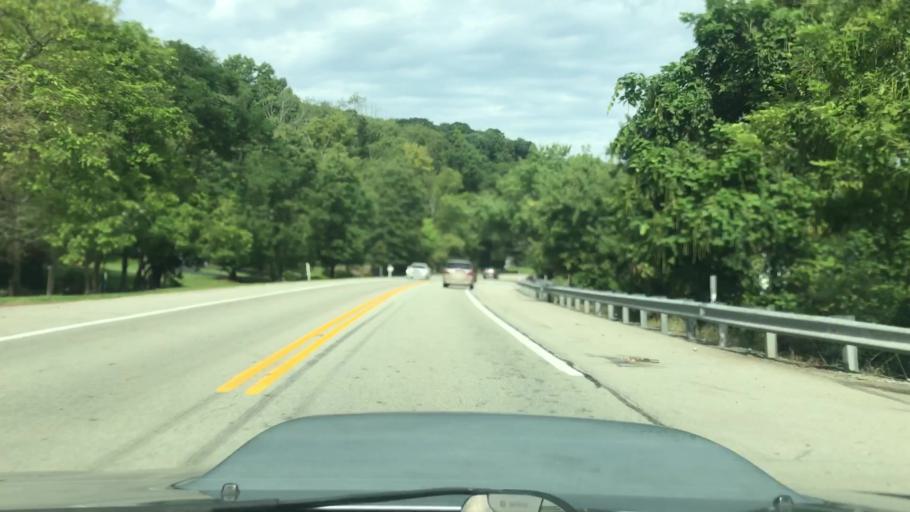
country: US
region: Pennsylvania
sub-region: Allegheny County
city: Oakmont
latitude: 40.5615
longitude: -79.8558
